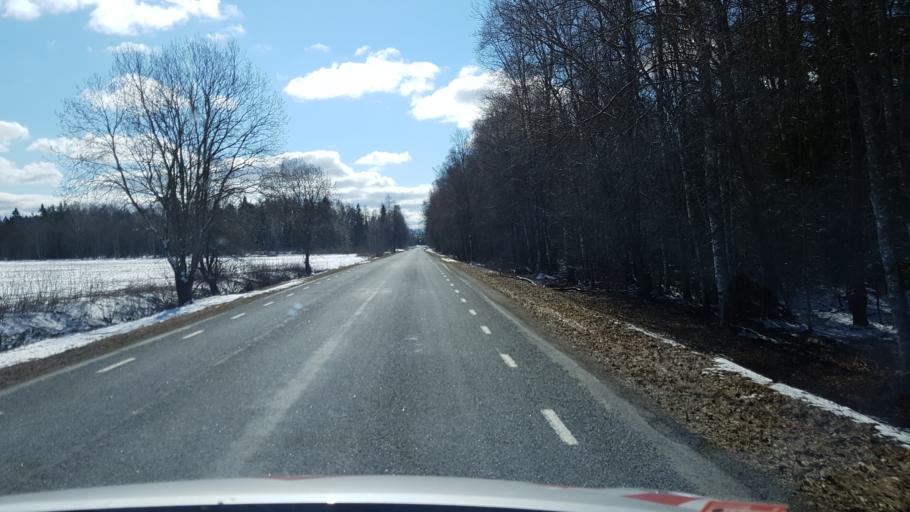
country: EE
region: Laeaene-Virumaa
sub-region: Kadrina vald
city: Kadrina
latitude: 59.4776
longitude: 25.9957
